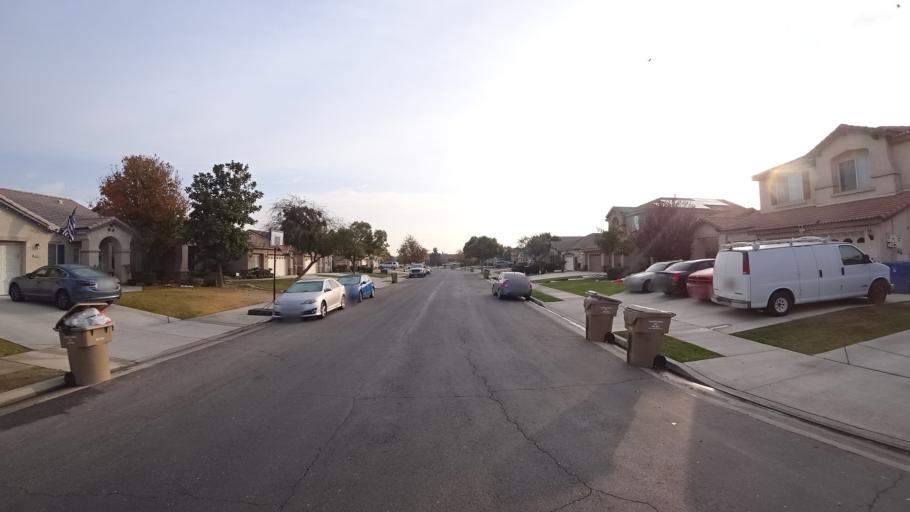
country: US
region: California
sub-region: Kern County
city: Greenacres
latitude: 35.4203
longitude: -119.1243
